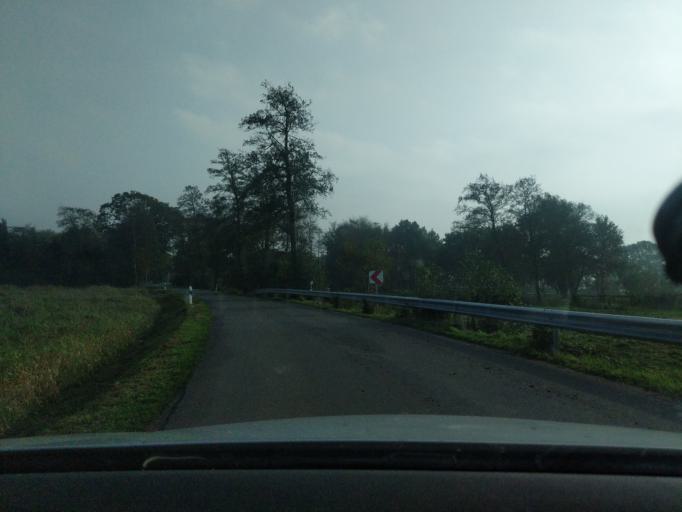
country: DE
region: Lower Saxony
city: Wanna
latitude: 53.7655
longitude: 8.7326
